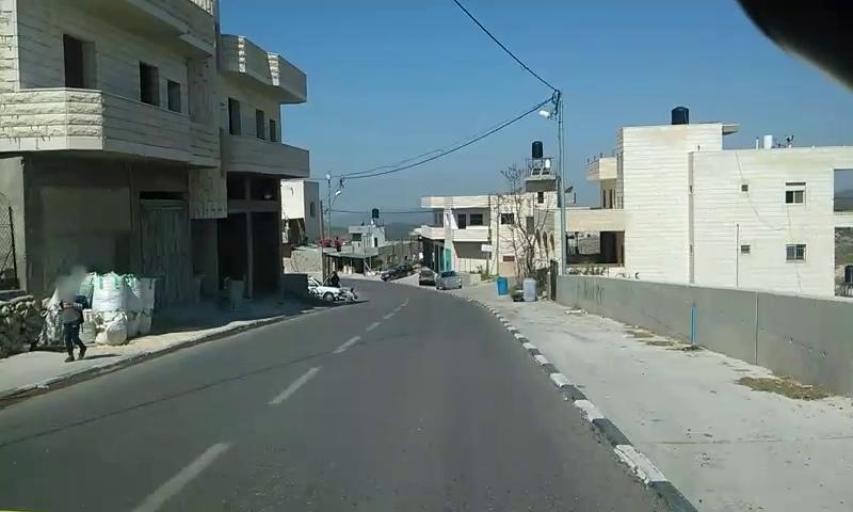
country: PS
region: West Bank
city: Husan
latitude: 31.7074
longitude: 35.1420
